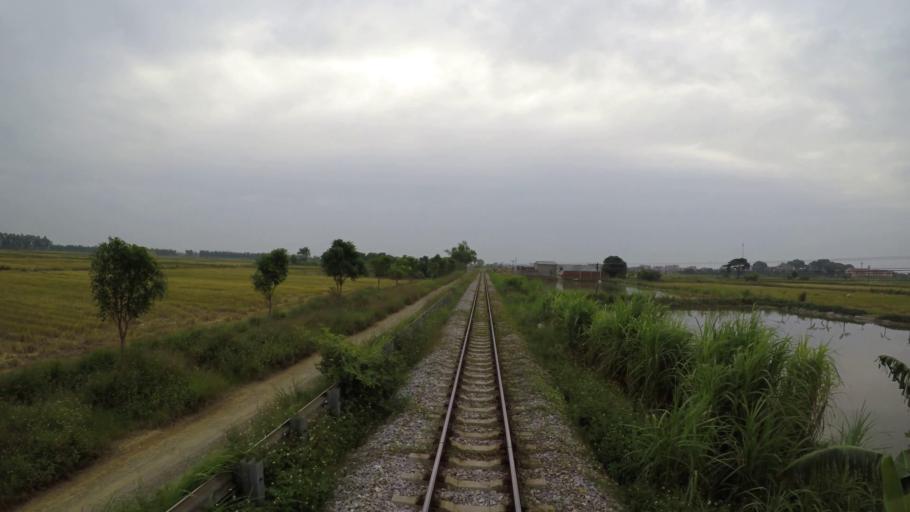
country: VN
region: Bac Ninh
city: Thua
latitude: 20.9638
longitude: 106.1777
